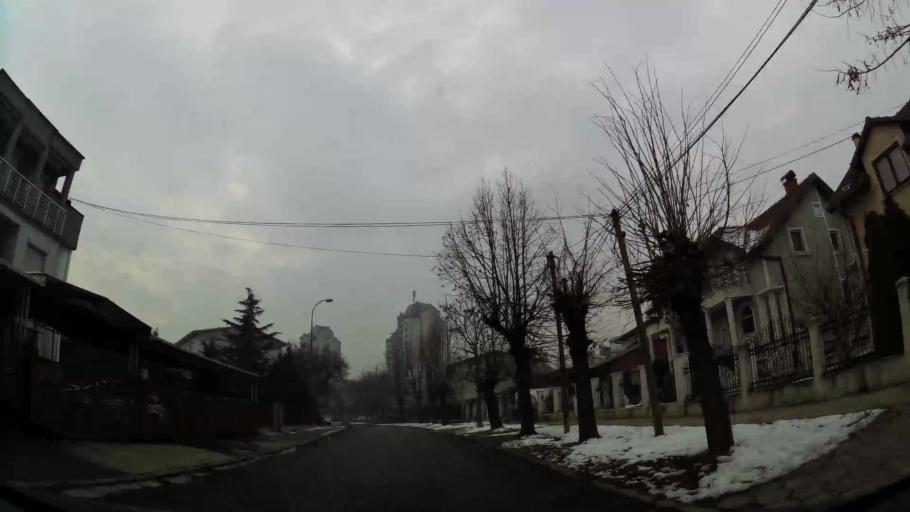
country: MK
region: Cair
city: Cair
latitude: 42.0130
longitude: 21.4602
